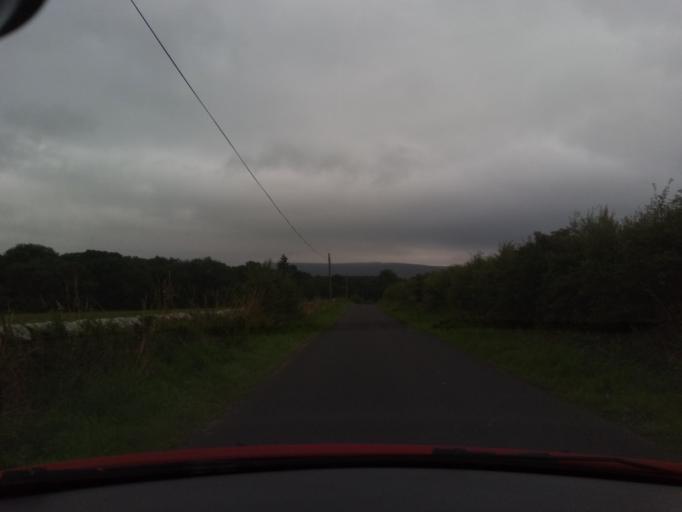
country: GB
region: England
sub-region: Northumberland
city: Otterburn
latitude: 55.3055
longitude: -2.0575
